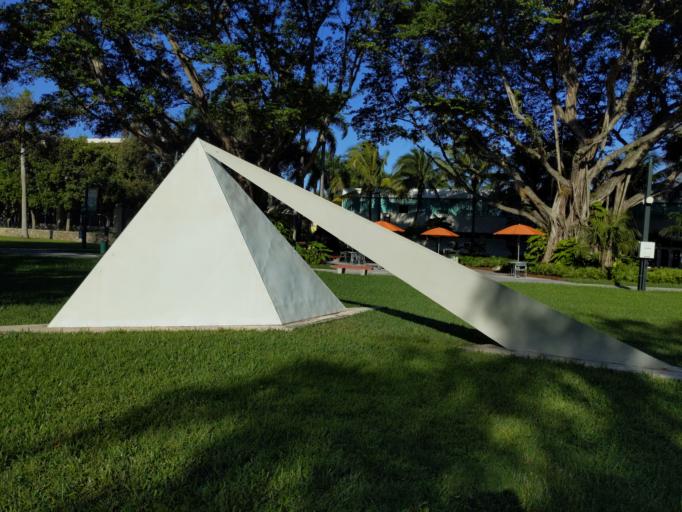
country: US
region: Florida
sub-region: Miami-Dade County
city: Coral Gables
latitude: 25.7213
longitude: -80.2775
